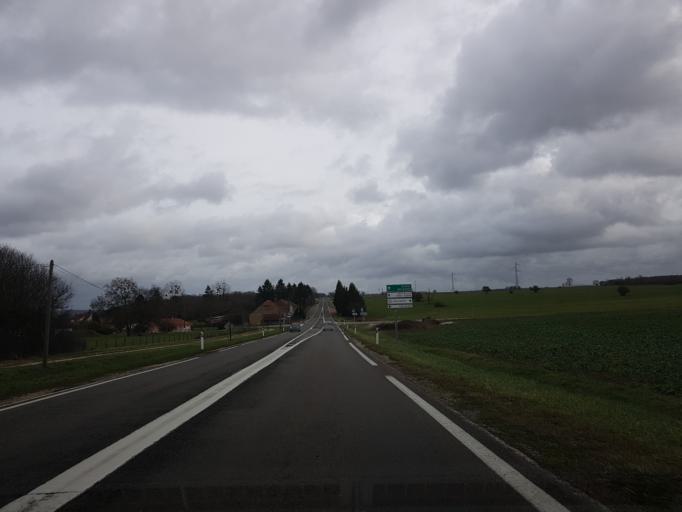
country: FR
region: Champagne-Ardenne
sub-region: Departement de la Haute-Marne
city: Chalindrey
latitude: 47.8179
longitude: 5.4889
